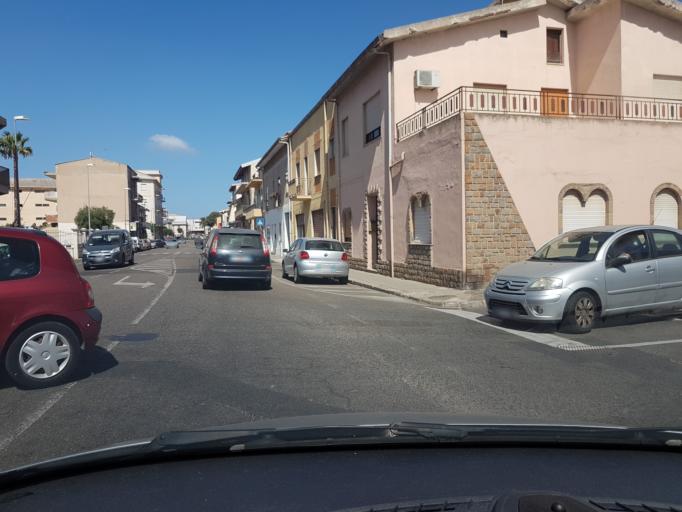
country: IT
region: Sardinia
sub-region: Provincia di Oristano
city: Oristano
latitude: 39.9077
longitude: 8.5992
